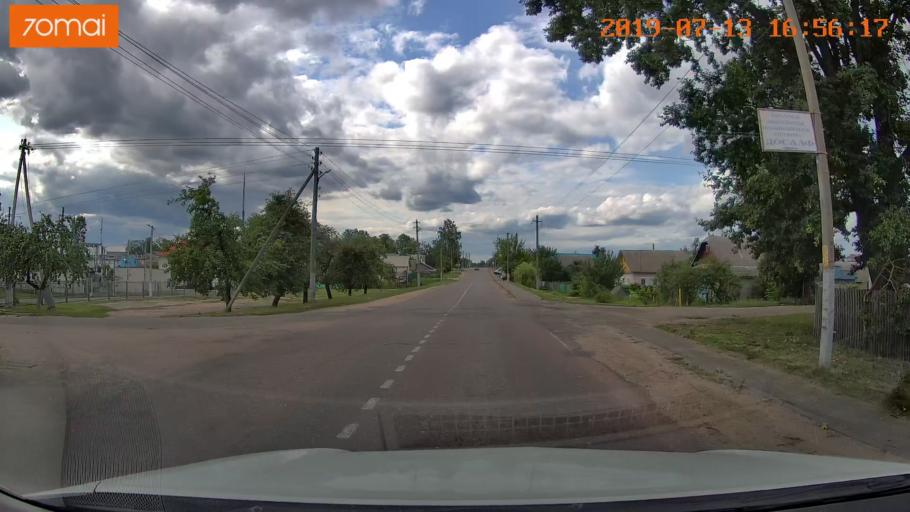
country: BY
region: Mogilev
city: Kirawsk
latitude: 53.2724
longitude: 29.4603
